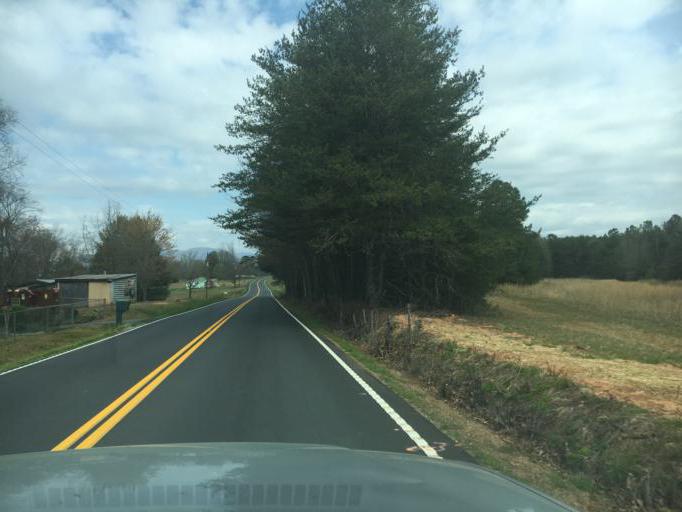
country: US
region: South Carolina
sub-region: Spartanburg County
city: Landrum
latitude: 35.0958
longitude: -82.2039
